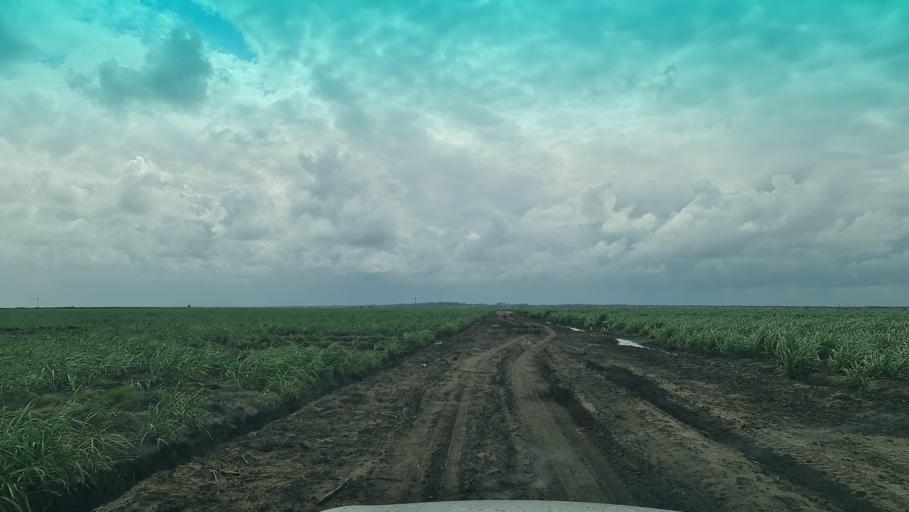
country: MZ
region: Maputo
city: Manhica
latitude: -25.4539
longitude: 32.8368
